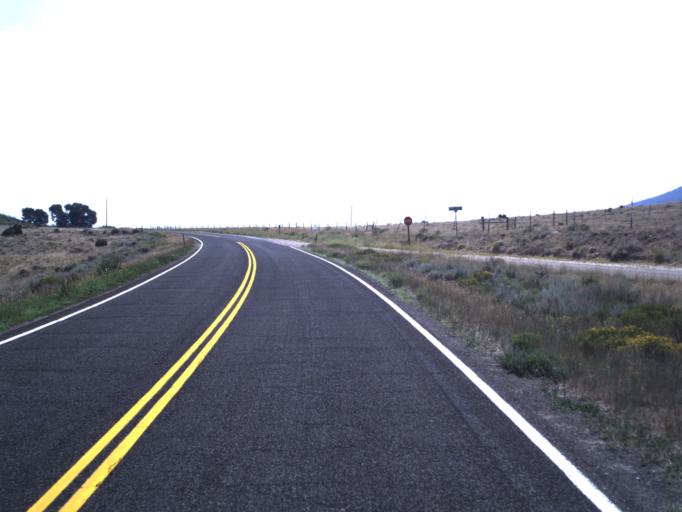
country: US
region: Utah
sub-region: Daggett County
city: Manila
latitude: 40.9764
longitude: -109.8298
